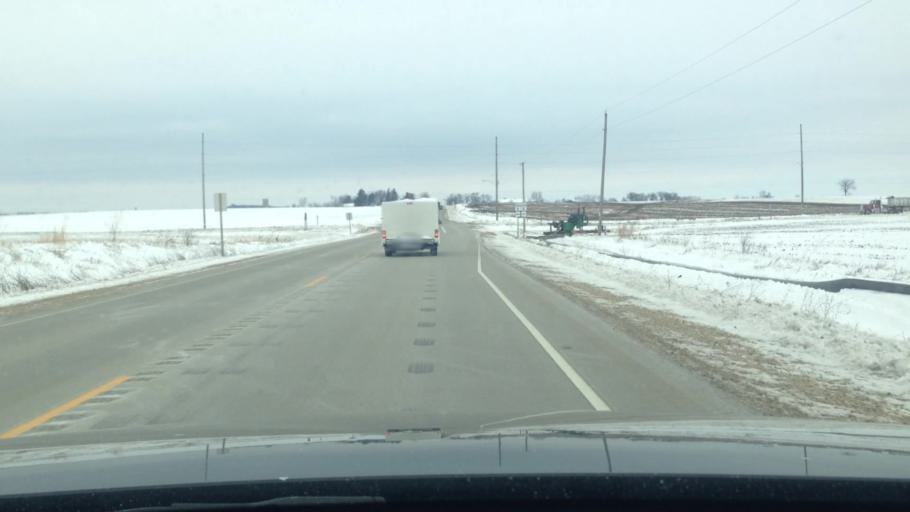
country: US
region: Illinois
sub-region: McHenry County
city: Hebron
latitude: 42.5148
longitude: -88.4427
